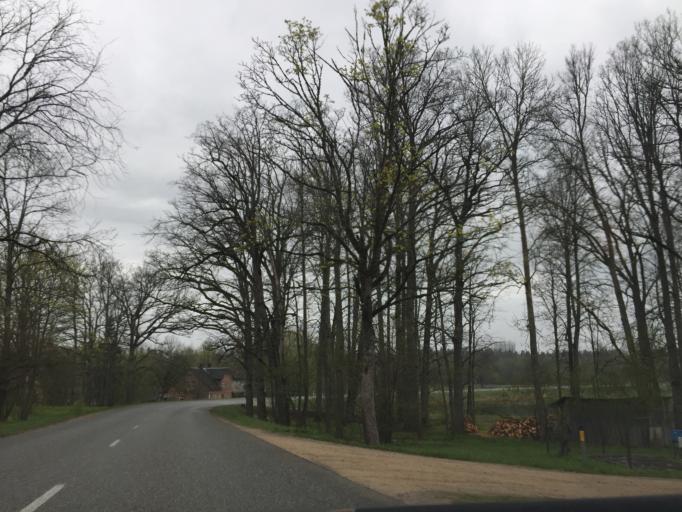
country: LV
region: Sigulda
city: Sigulda
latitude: 57.0278
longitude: 24.8165
